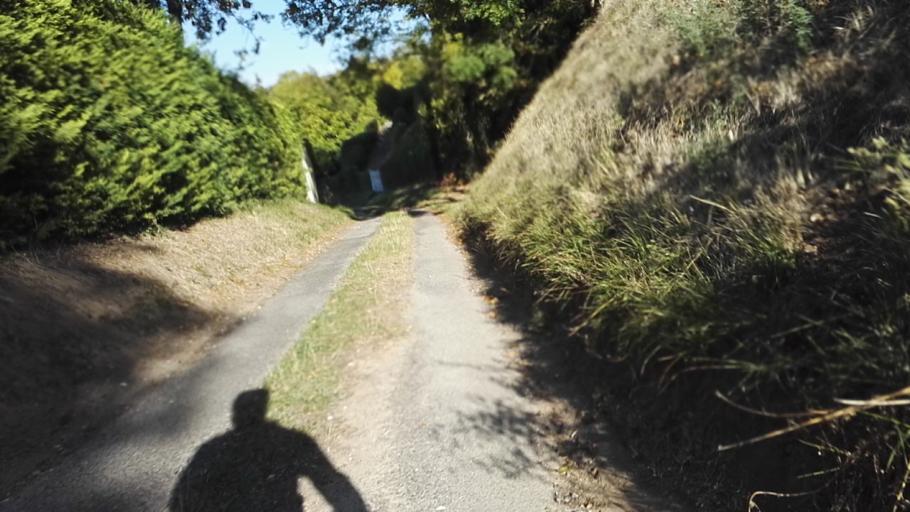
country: FR
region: Haute-Normandie
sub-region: Departement de l'Eure
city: Houlbec-Cocherel
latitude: 49.0561
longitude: 1.3359
